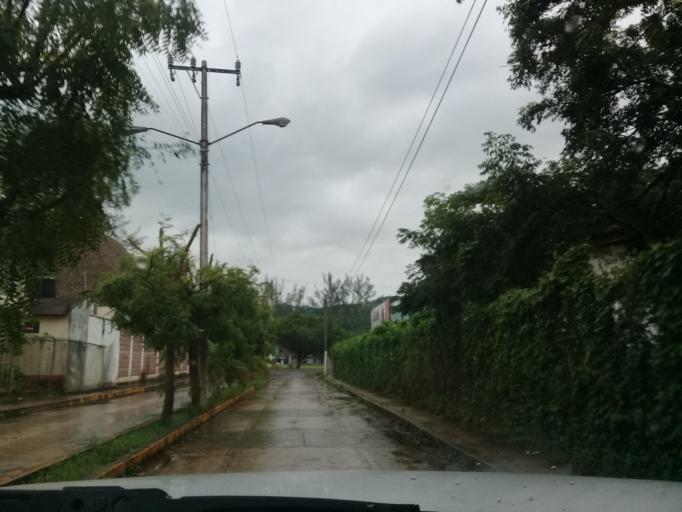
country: MX
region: Veracruz
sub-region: San Andres Tuxtla
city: Cerro las Iguanas
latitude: 18.4246
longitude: -95.2187
